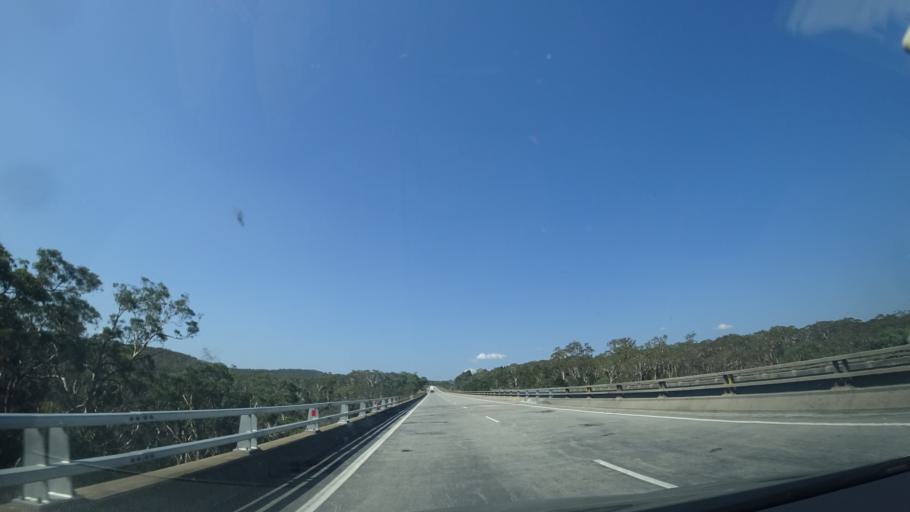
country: AU
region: New South Wales
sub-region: Wingecarribee
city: Moss Vale
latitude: -34.4753
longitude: 150.3218
